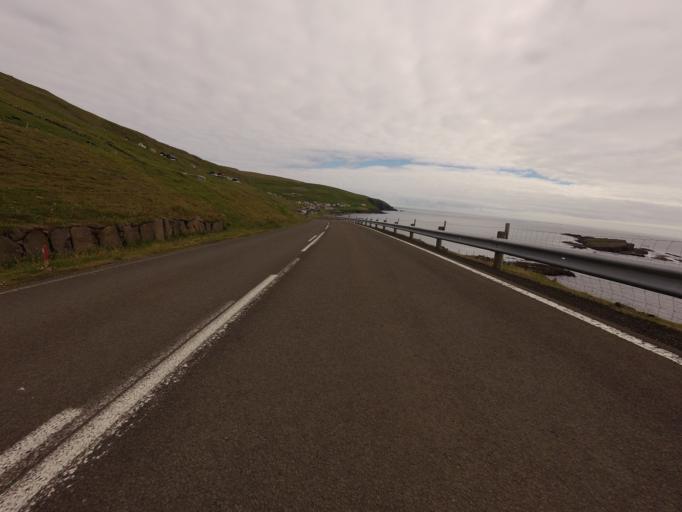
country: FO
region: Suduroy
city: Vagur
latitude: 61.4076
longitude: -6.7322
